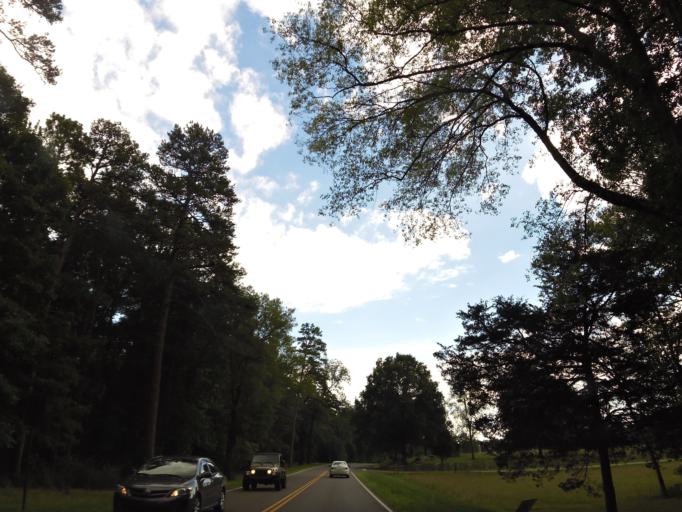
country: US
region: Georgia
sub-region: Catoosa County
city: Fort Oglethorpe
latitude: 34.9191
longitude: -85.2608
